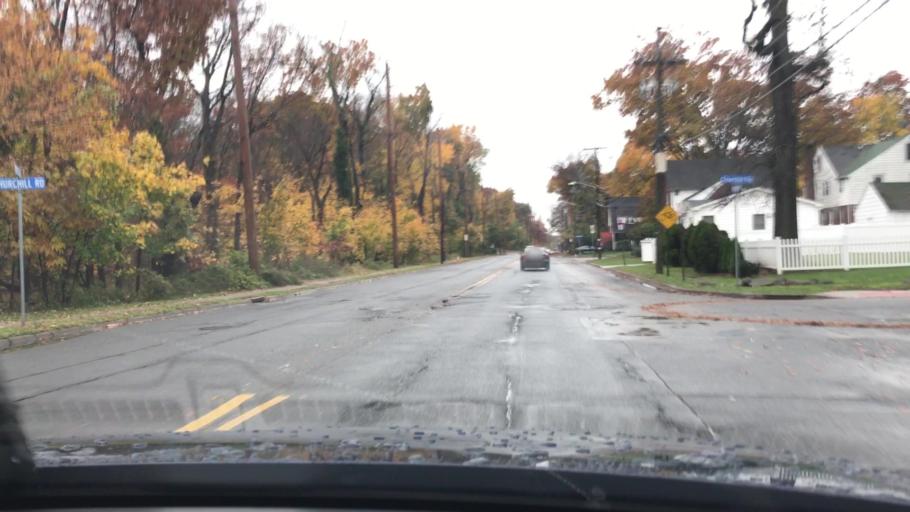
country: US
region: New Jersey
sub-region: Bergen County
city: Teaneck
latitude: 40.9072
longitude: -74.0048
